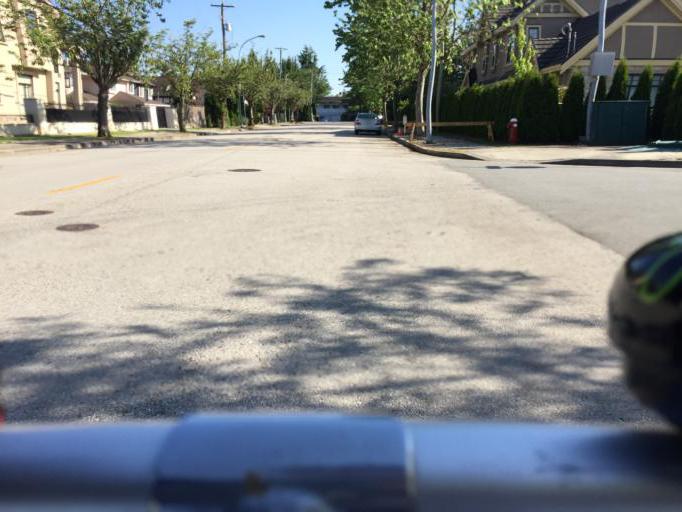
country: CA
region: British Columbia
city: Richmond
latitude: 49.1495
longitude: -123.1310
